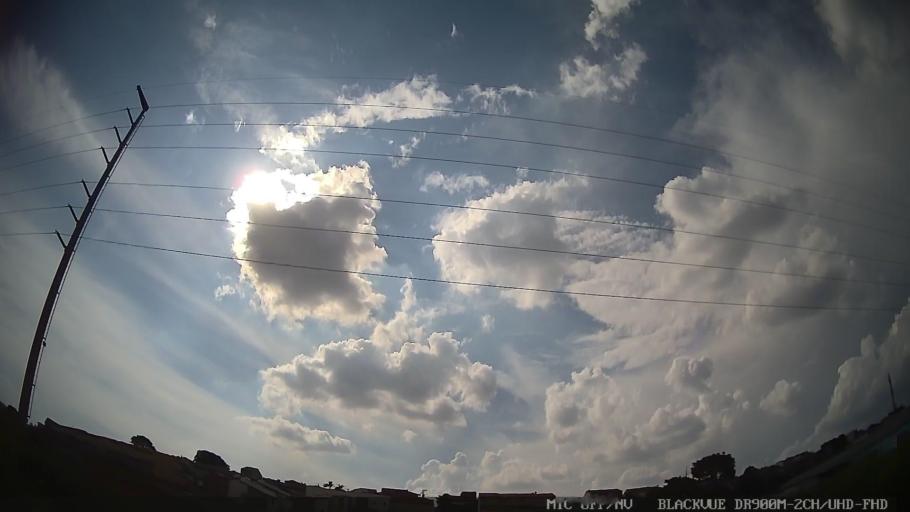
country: BR
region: Sao Paulo
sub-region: Braganca Paulista
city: Braganca Paulista
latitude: -22.9203
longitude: -46.5510
